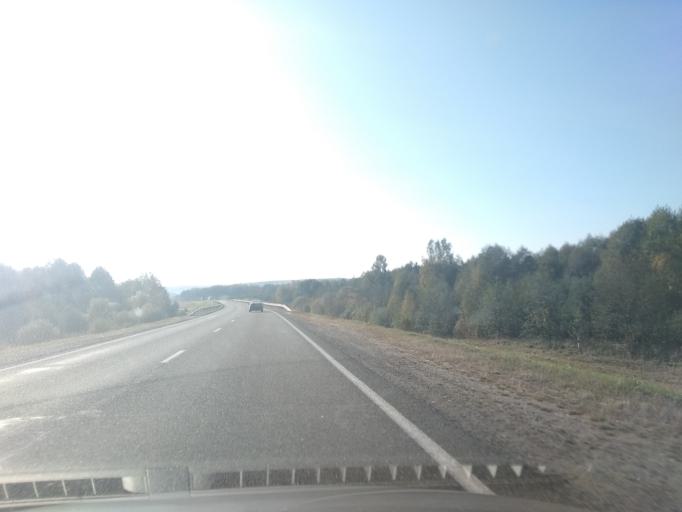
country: BY
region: Grodnenskaya
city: Zhyrovichy
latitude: 53.0614
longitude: 25.3925
